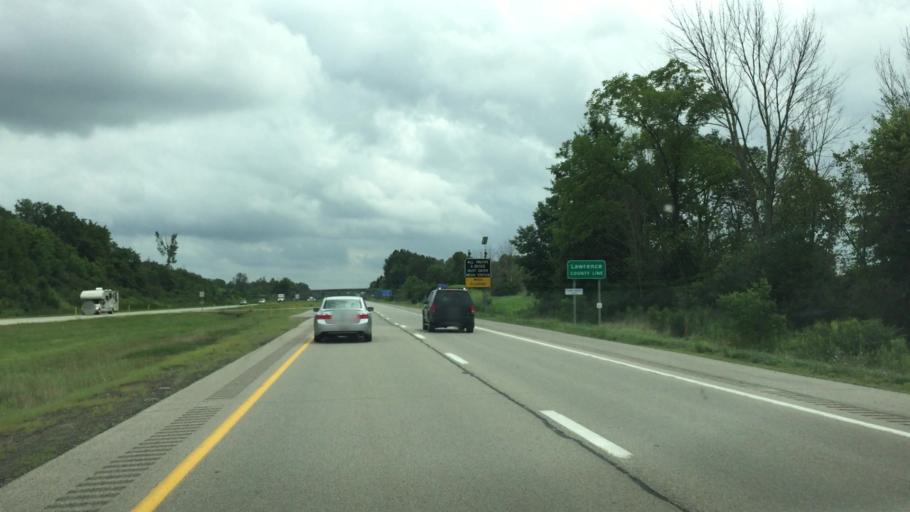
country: US
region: Pennsylvania
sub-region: Mercer County
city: Grove City
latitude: 41.1131
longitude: -80.1464
